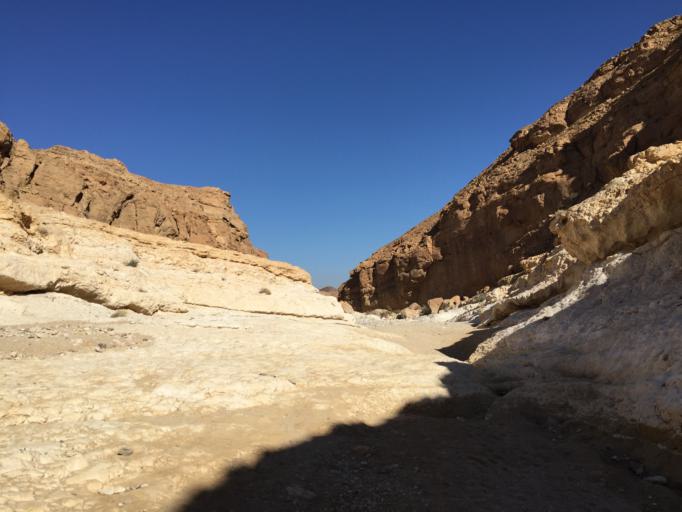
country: IL
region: Southern District
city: Mitzpe Ramon
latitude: 30.5990
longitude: 34.9464
